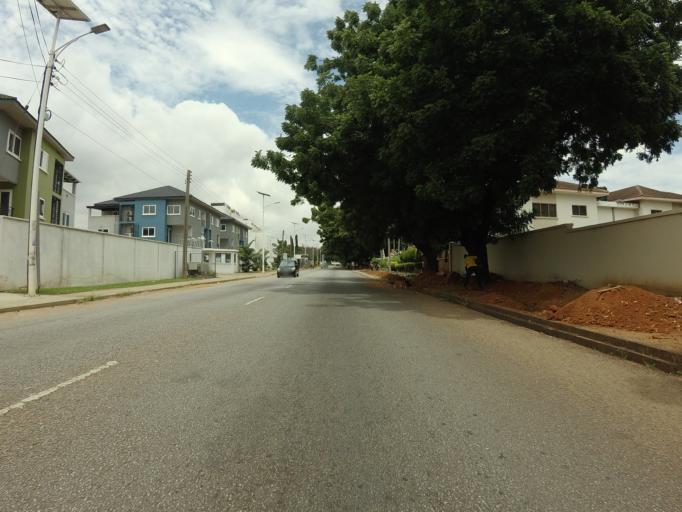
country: GH
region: Greater Accra
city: Accra
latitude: 5.5785
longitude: -0.1769
